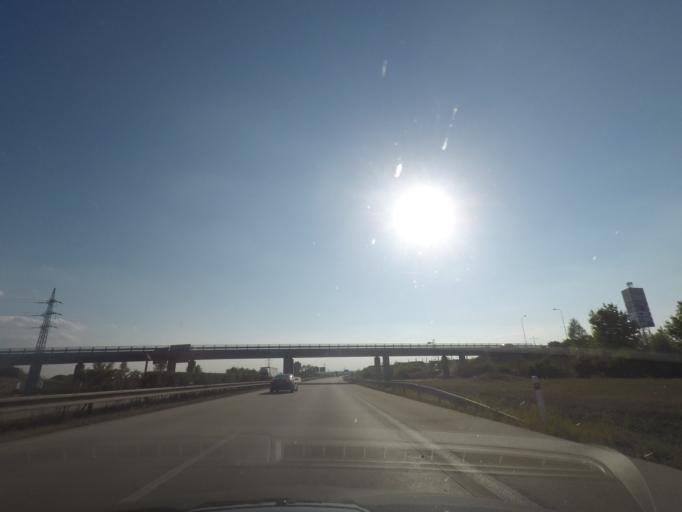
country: CZ
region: Olomoucky
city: Grygov
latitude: 49.5590
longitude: 17.3127
